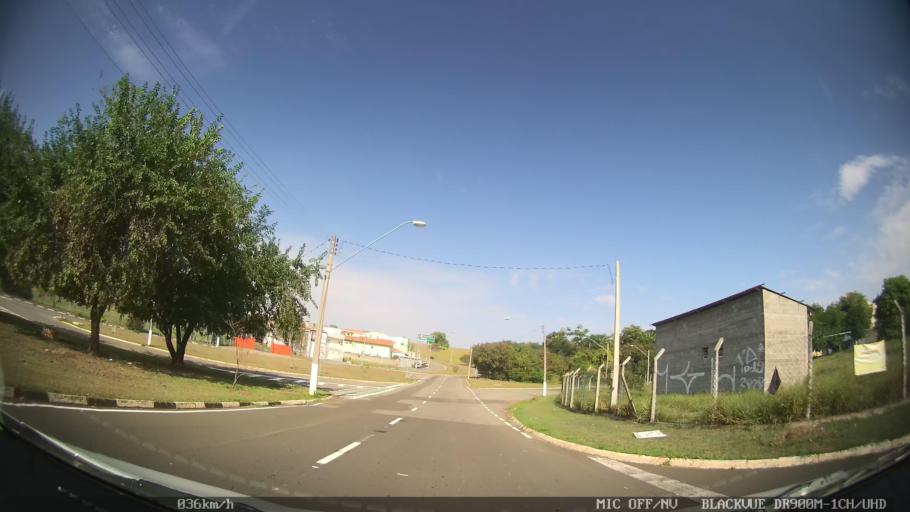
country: BR
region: Sao Paulo
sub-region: Paulinia
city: Paulinia
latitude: -22.7785
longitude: -47.1650
